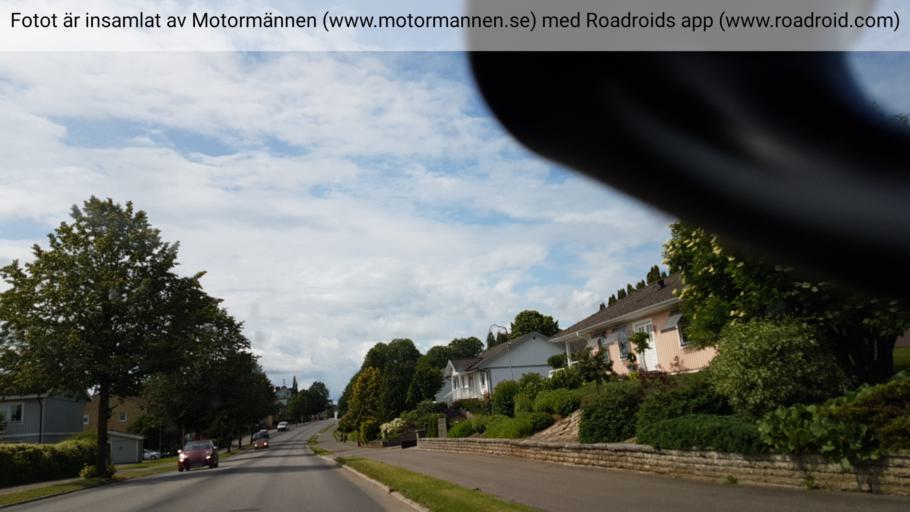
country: SE
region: Vaestra Goetaland
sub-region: Falkopings Kommun
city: Falkoeping
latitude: 58.1827
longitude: 13.5527
